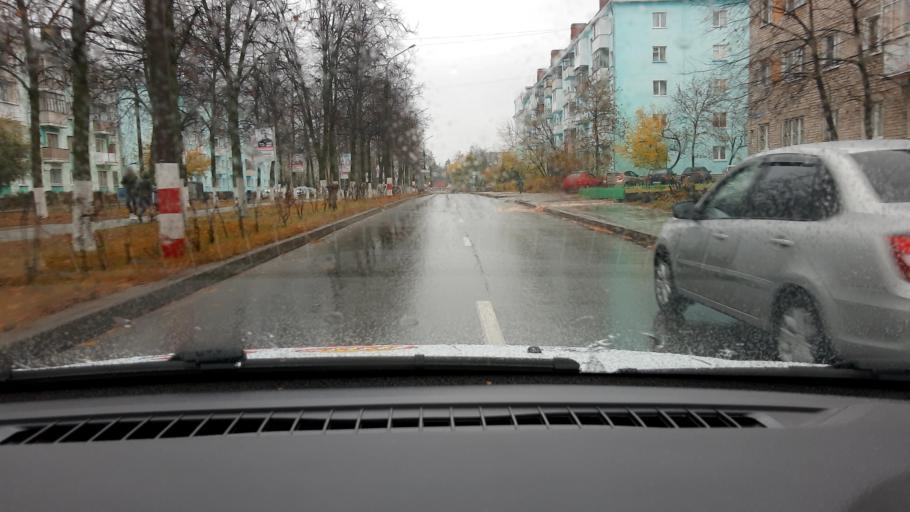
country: RU
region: Nizjnij Novgorod
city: Dzerzhinsk
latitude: 56.2403
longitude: 43.4444
